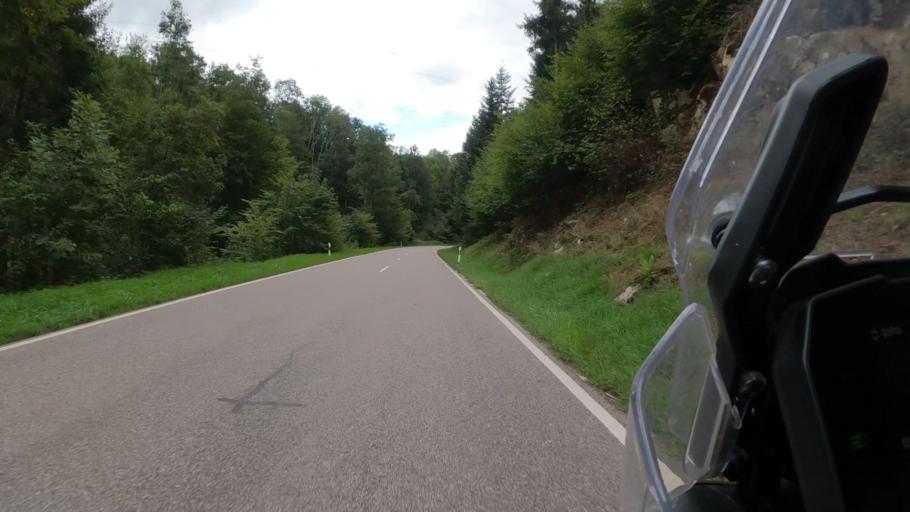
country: DE
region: Baden-Wuerttemberg
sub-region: Freiburg Region
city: Uhlingen-Birkendorf
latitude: 47.7092
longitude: 8.3441
